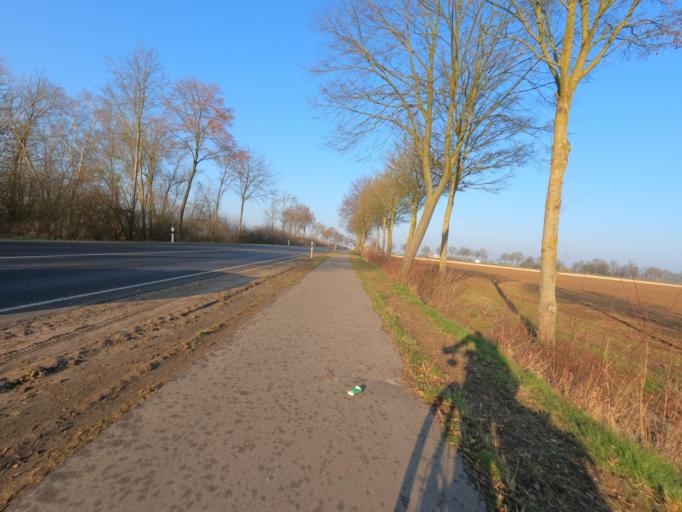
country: DE
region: North Rhine-Westphalia
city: Erkelenz
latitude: 51.0898
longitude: 6.2809
